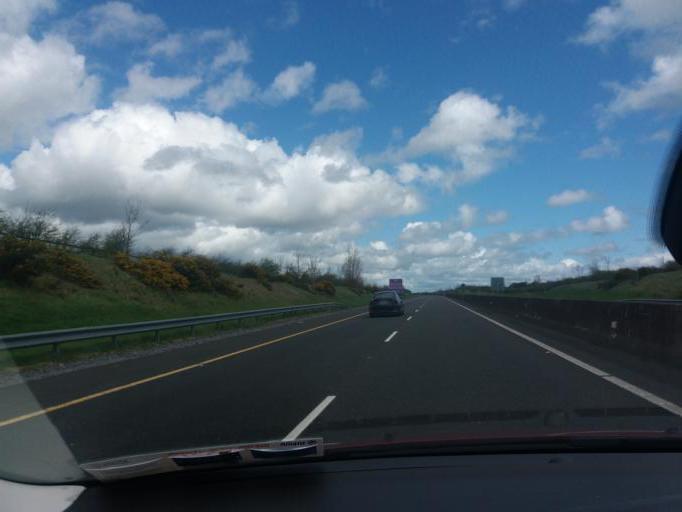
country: IE
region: Leinster
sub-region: Laois
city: Rathdowney
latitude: 52.7651
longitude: -7.5513
